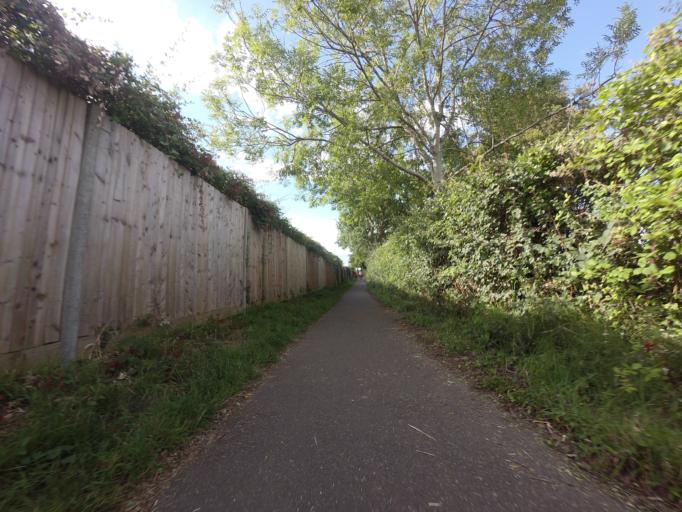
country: GB
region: England
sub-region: East Sussex
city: Hailsham
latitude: 50.8682
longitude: 0.2539
